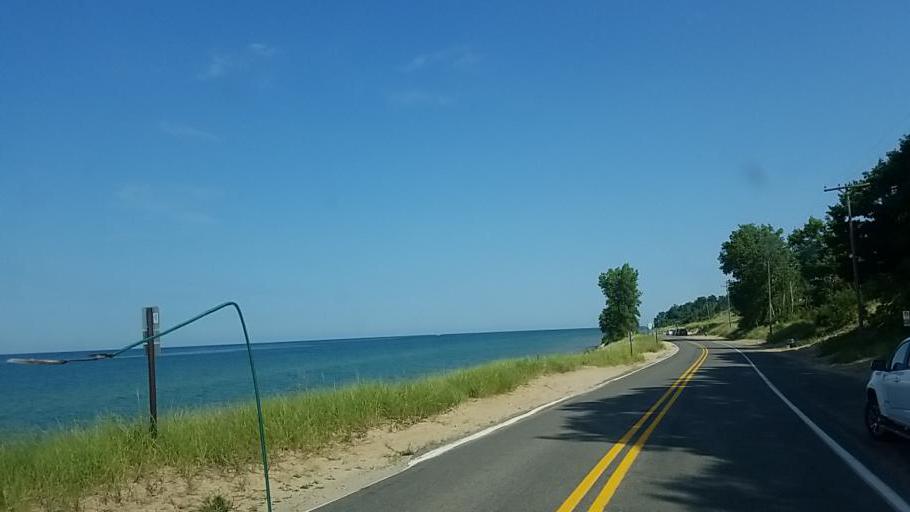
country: US
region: Michigan
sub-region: Muskegon County
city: Whitehall
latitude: 43.3388
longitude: -86.4073
